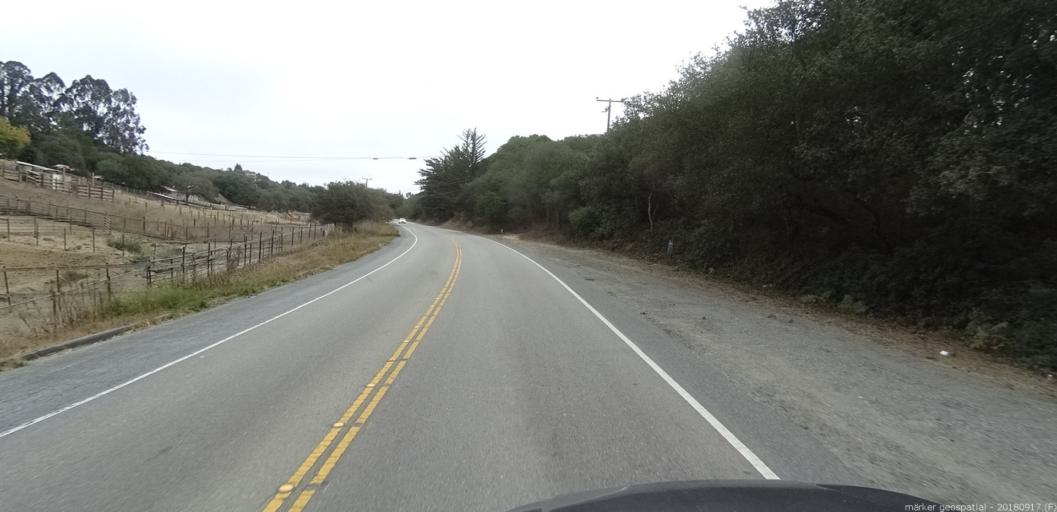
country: US
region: California
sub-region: Monterey County
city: Prunedale
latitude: 36.8001
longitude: -121.6892
